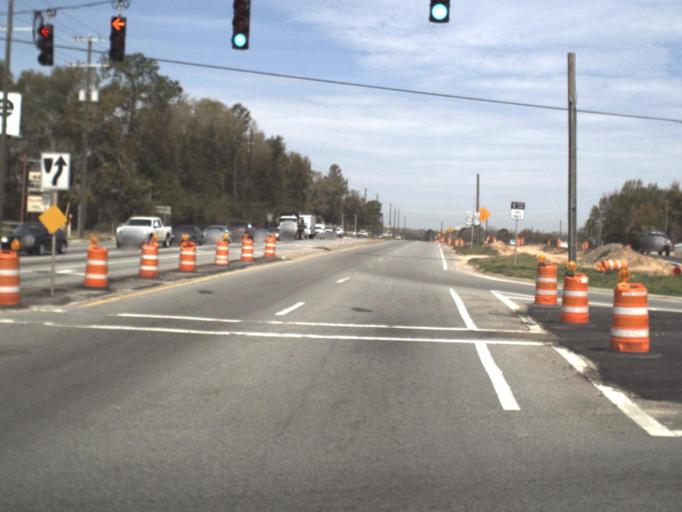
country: US
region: Florida
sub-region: Leon County
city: Tallahassee
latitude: 30.4353
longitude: -84.3529
